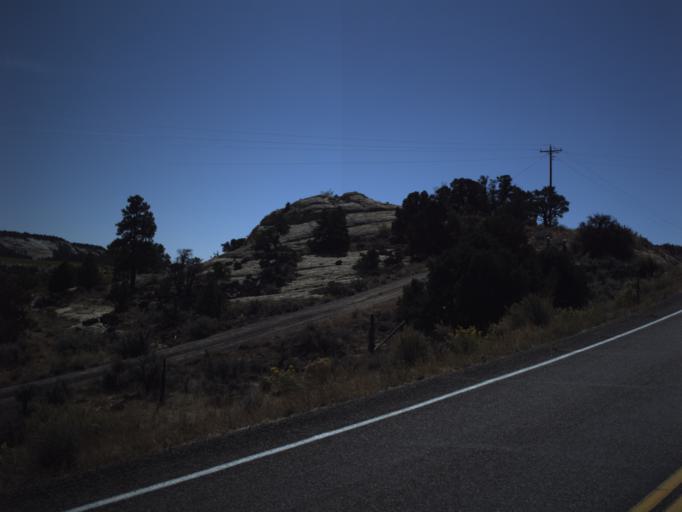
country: US
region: Utah
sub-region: Wayne County
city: Loa
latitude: 37.9003
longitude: -111.4378
